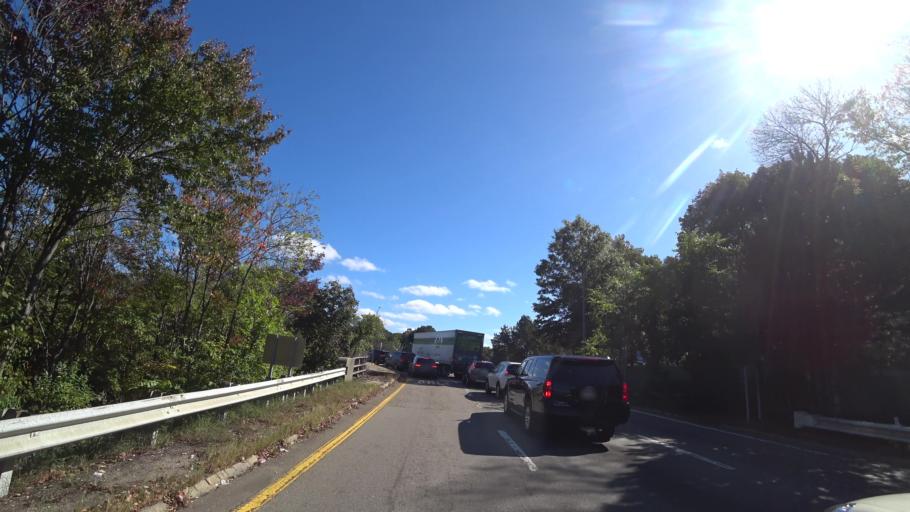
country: US
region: Massachusetts
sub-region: Norfolk County
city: Braintree
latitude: 42.2257
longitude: -71.0055
